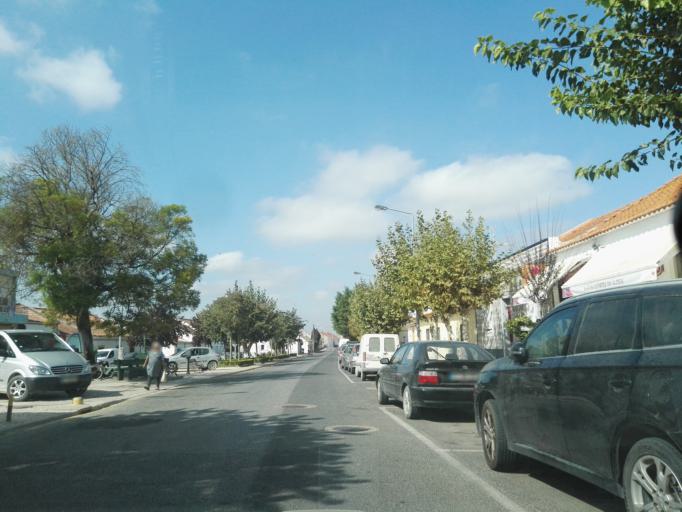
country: PT
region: Santarem
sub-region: Benavente
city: Poceirao
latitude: 38.8602
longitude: -8.7459
